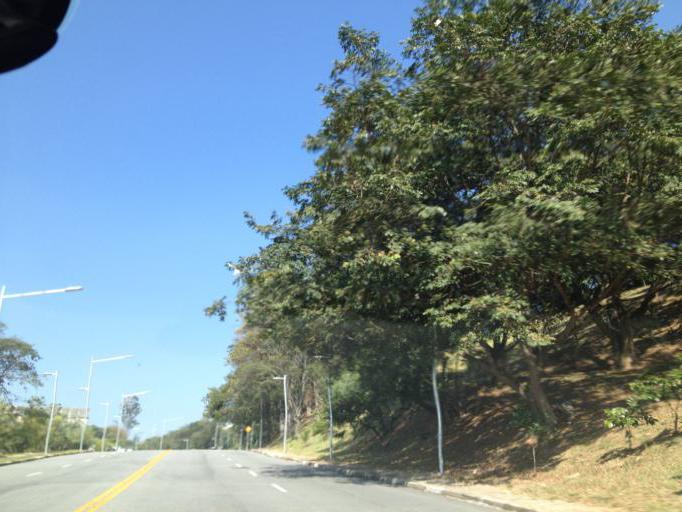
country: BR
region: Sao Paulo
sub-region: Osasco
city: Osasco
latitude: -23.5616
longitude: -46.7422
